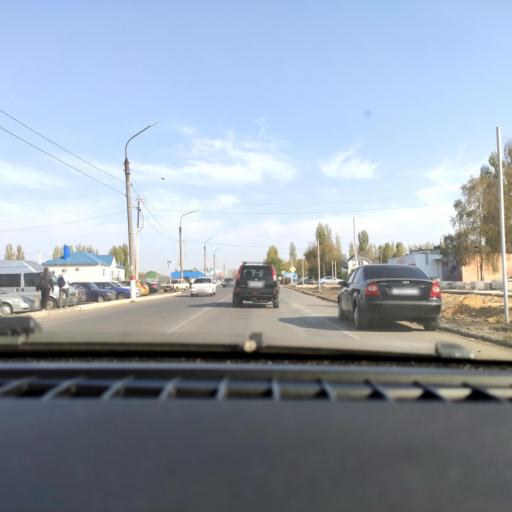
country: RU
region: Voronezj
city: Novaya Usman'
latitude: 51.6474
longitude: 39.4182
